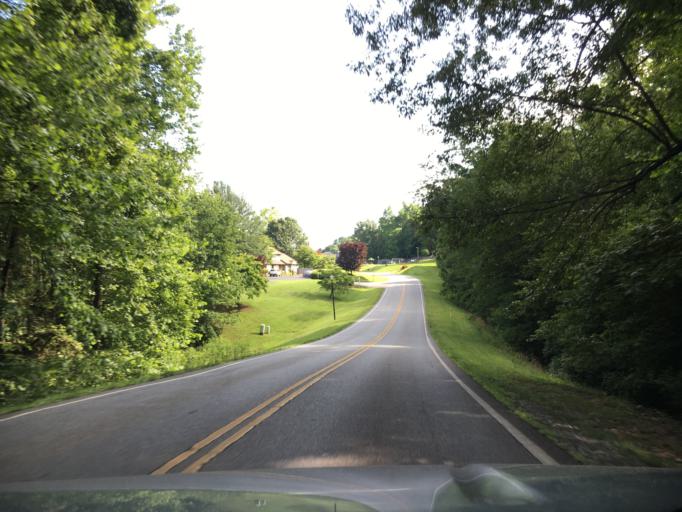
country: US
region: Virginia
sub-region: Bedford County
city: Forest
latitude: 37.3908
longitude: -79.2557
